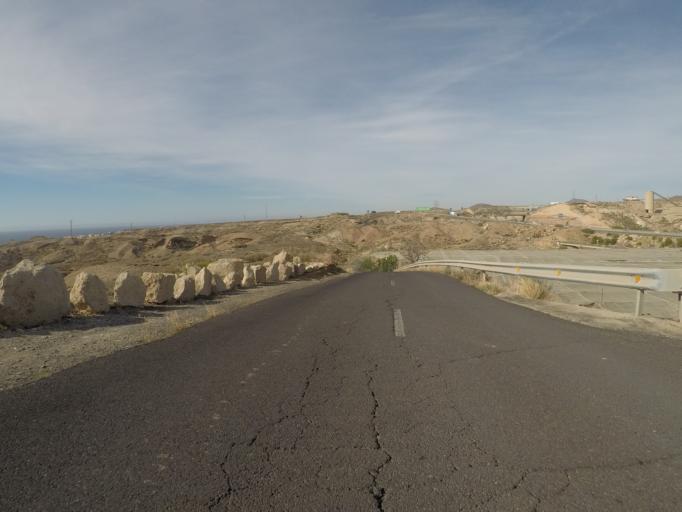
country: ES
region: Canary Islands
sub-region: Provincia de Santa Cruz de Tenerife
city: Lomo de Arico
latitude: 28.1190
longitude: -16.4717
